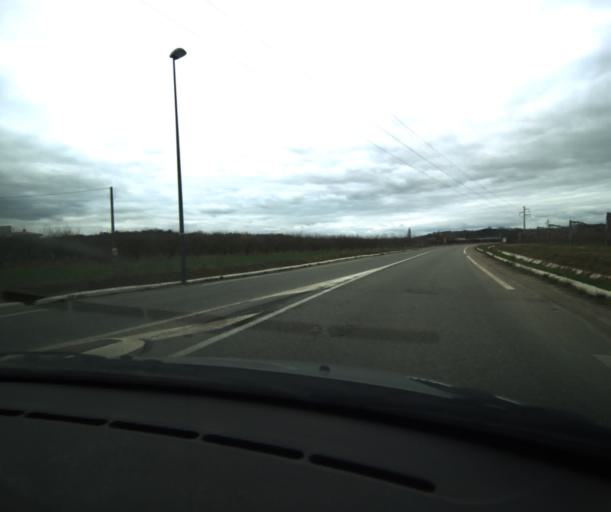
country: FR
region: Midi-Pyrenees
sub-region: Departement du Tarn-et-Garonne
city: Moissac
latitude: 44.0998
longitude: 1.1130
